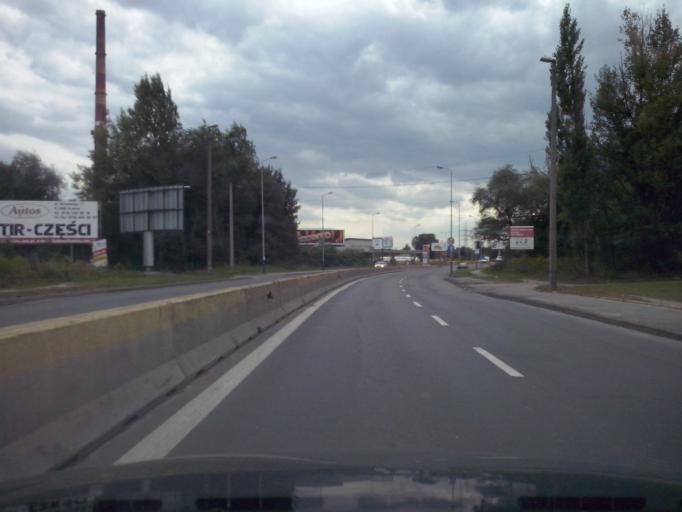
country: PL
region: Lesser Poland Voivodeship
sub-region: Krakow
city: Krakow
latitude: 50.0596
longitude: 20.0032
